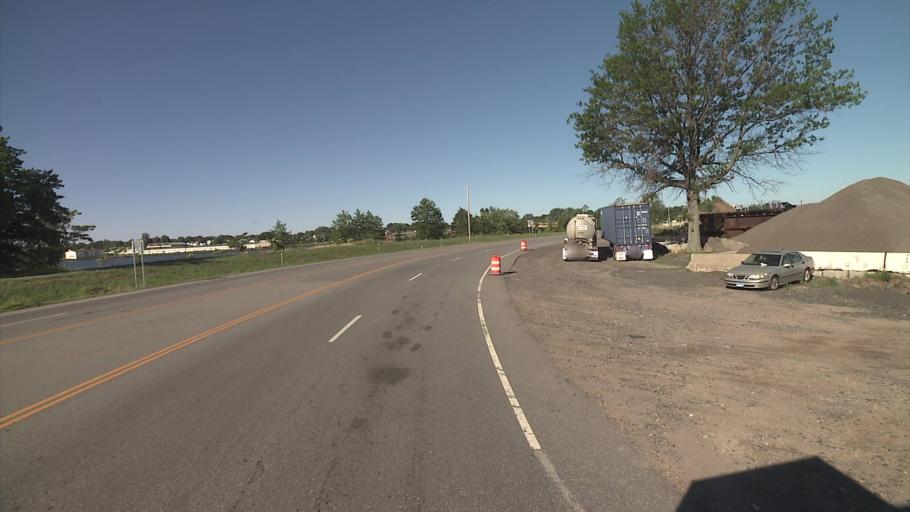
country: US
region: Connecticut
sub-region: New Haven County
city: West Haven
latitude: 41.2828
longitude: -72.9350
